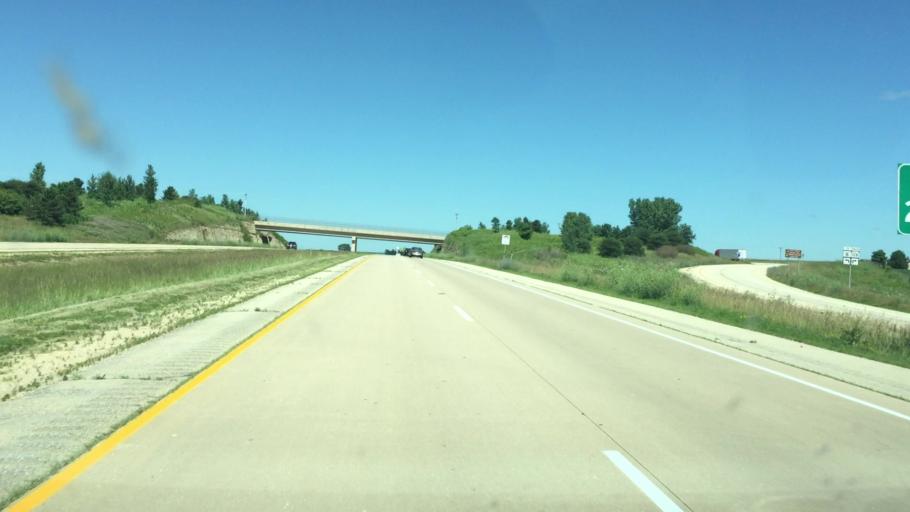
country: US
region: Wisconsin
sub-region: Grant County
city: Platteville
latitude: 42.7435
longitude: -90.3416
